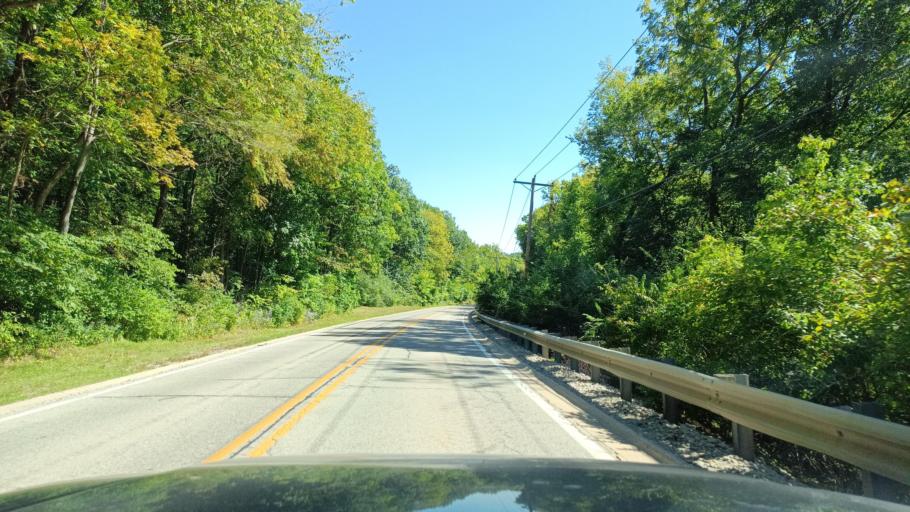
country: US
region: Illinois
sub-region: Woodford County
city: Eureka
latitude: 40.6271
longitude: -89.2497
